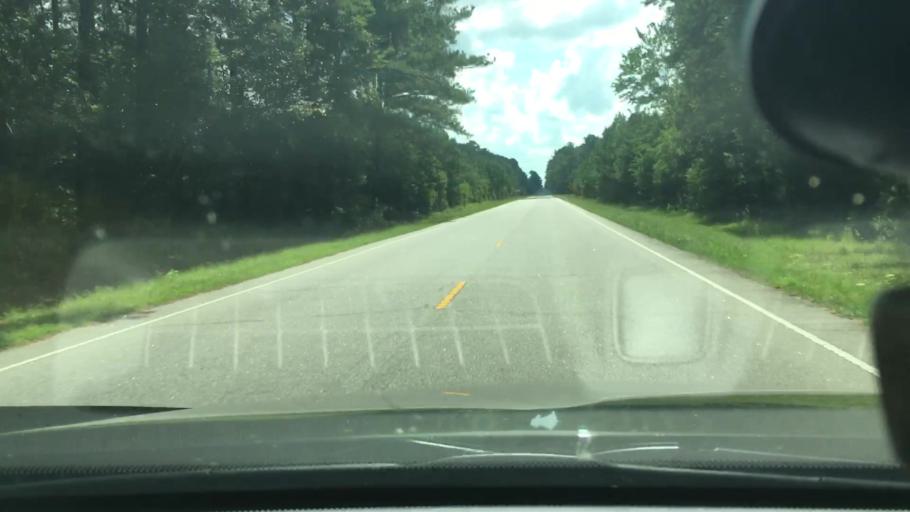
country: US
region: North Carolina
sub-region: Edgecombe County
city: Pinetops
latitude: 35.7633
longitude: -77.5606
